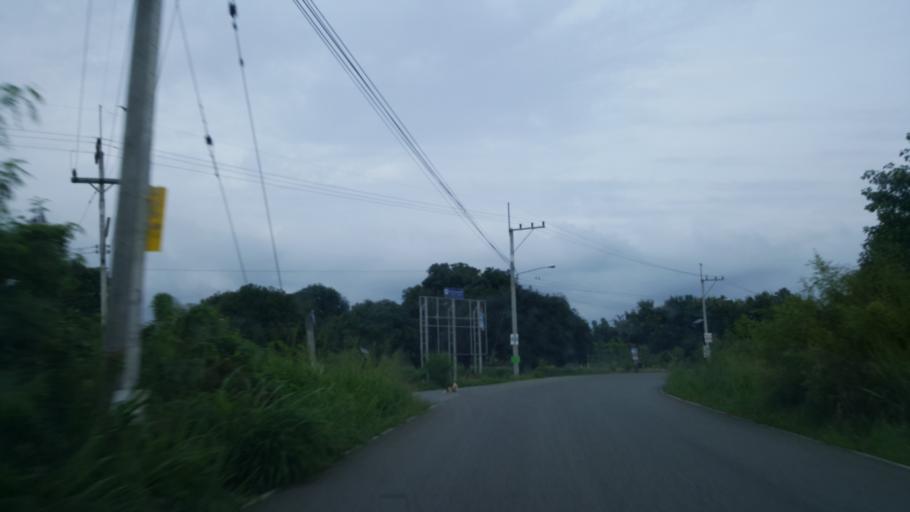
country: TH
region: Chon Buri
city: Sattahip
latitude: 12.6996
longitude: 100.9030
